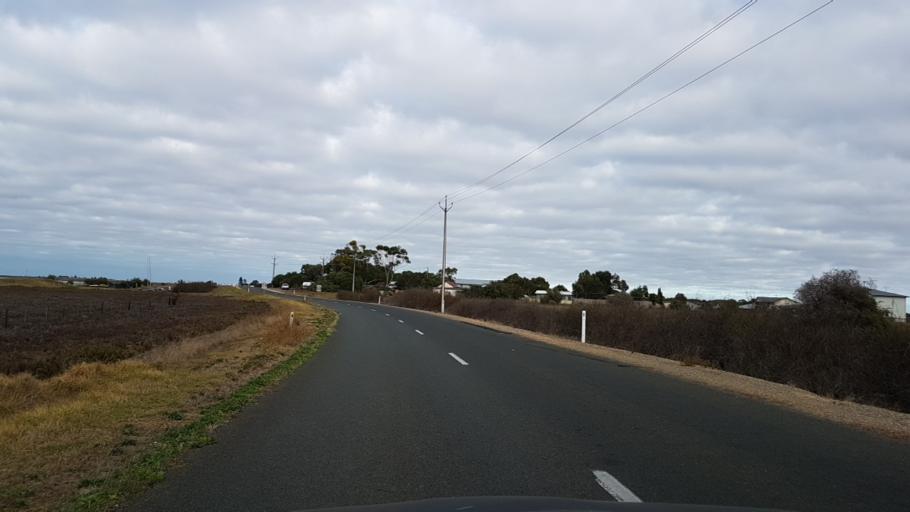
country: AU
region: South Australia
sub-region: Alexandrina
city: Langhorne Creek
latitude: -35.4004
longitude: 138.9837
